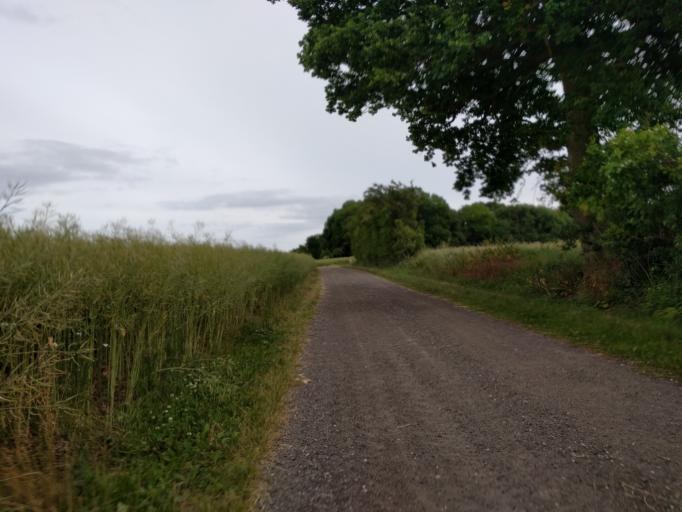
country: DK
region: South Denmark
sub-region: Kerteminde Kommune
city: Langeskov
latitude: 55.3966
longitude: 10.5827
